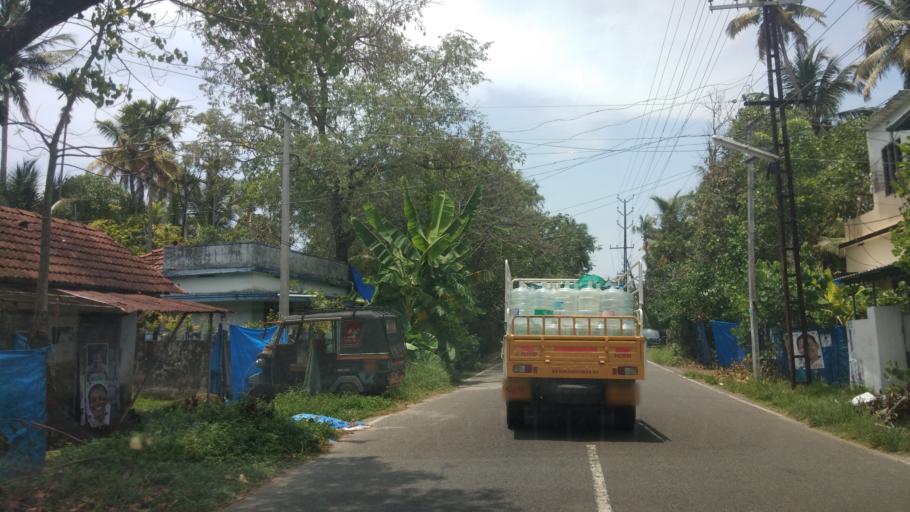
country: IN
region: Kerala
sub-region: Alappuzha
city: Kutiatodu
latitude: 9.8492
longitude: 76.2671
